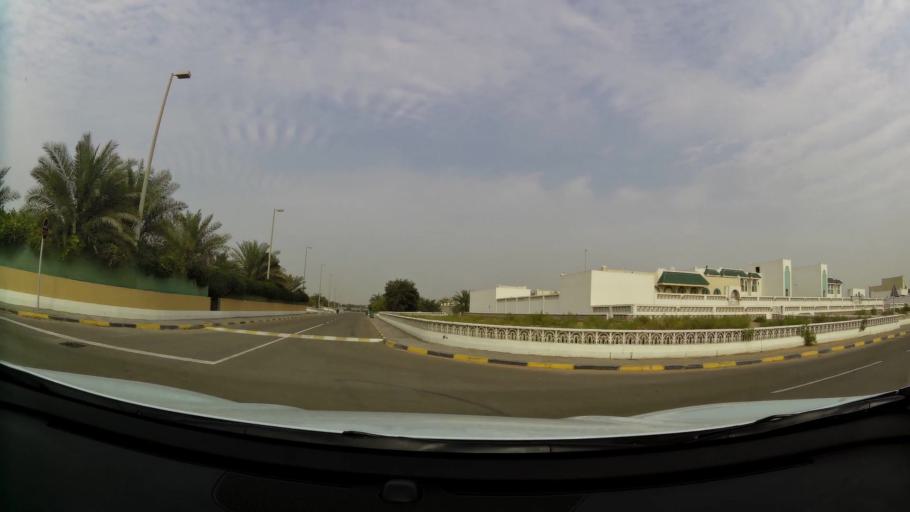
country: AE
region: Abu Dhabi
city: Abu Dhabi
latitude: 24.6792
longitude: 54.7579
